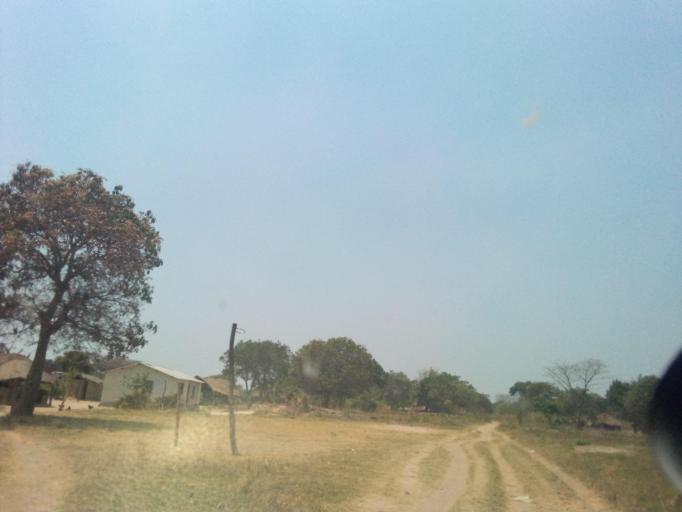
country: ZM
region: Copperbelt
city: Kataba
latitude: -12.2425
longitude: 30.3215
